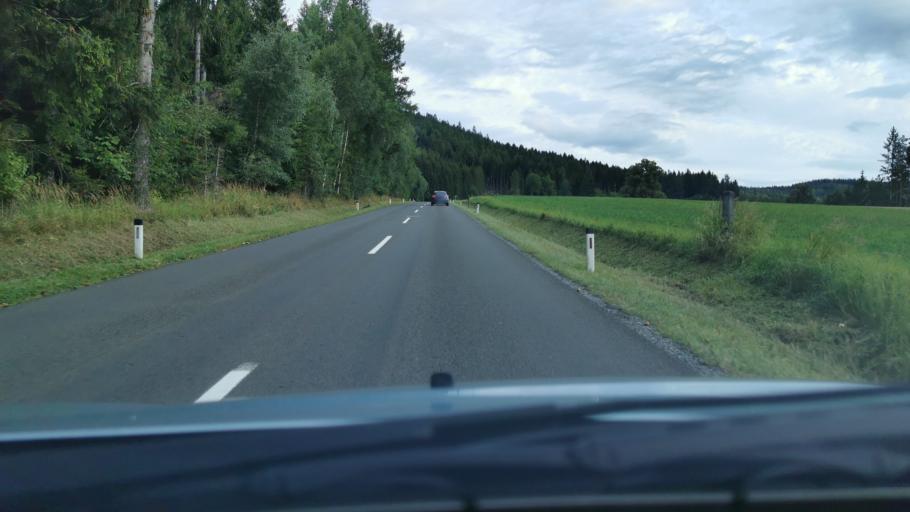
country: AT
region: Styria
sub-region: Politischer Bezirk Weiz
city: Fischbach
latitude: 47.3997
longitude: 15.6645
